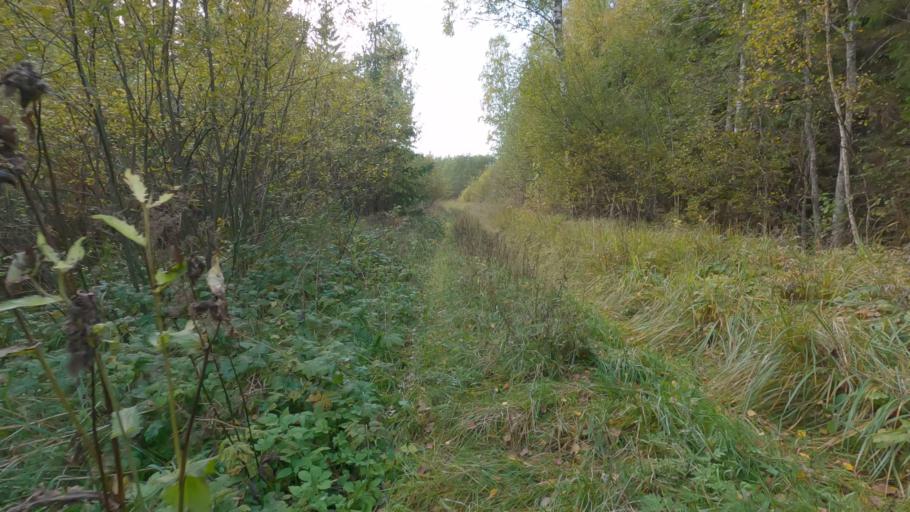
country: EE
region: Raplamaa
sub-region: Rapla vald
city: Rapla
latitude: 58.9722
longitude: 24.7738
